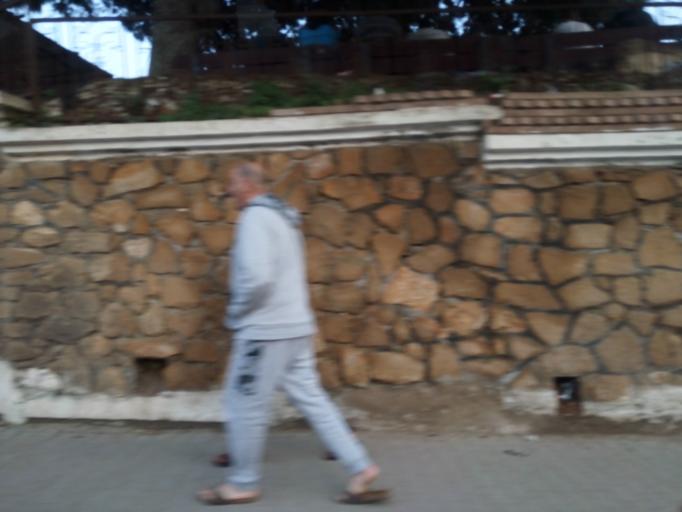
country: DZ
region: Tipaza
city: Bou Ismail
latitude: 36.6240
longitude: 2.6558
